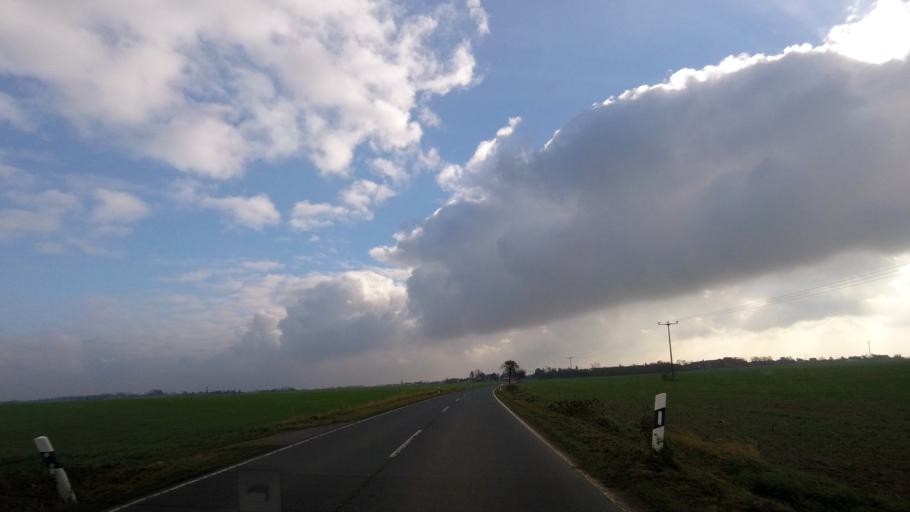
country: DE
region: Brandenburg
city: Niedergorsdorf
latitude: 51.9776
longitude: 12.9598
